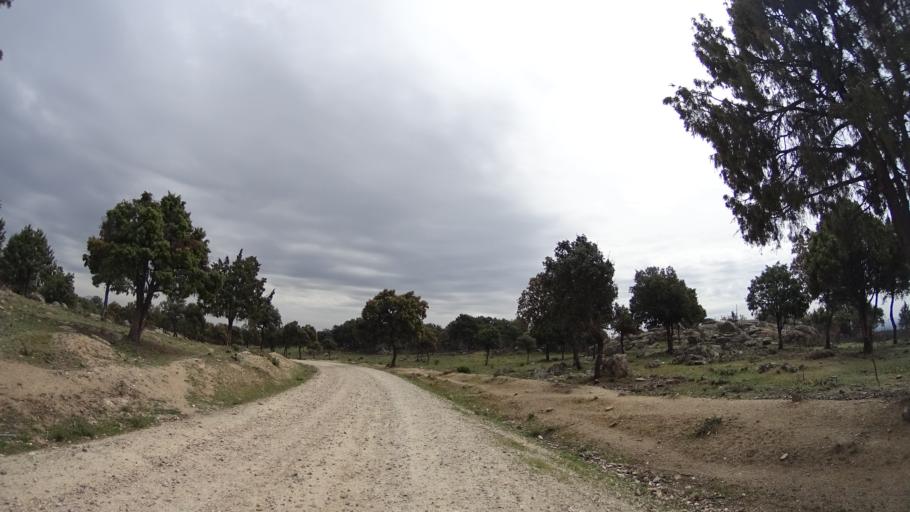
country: ES
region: Madrid
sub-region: Provincia de Madrid
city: Hoyo de Manzanares
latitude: 40.5998
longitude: -3.8837
